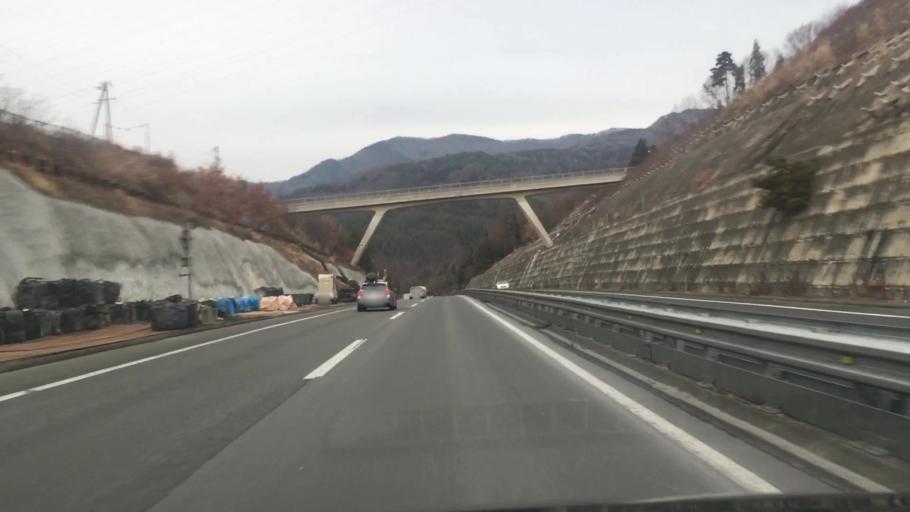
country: JP
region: Nagano
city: Ueda
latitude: 36.4653
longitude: 138.1981
